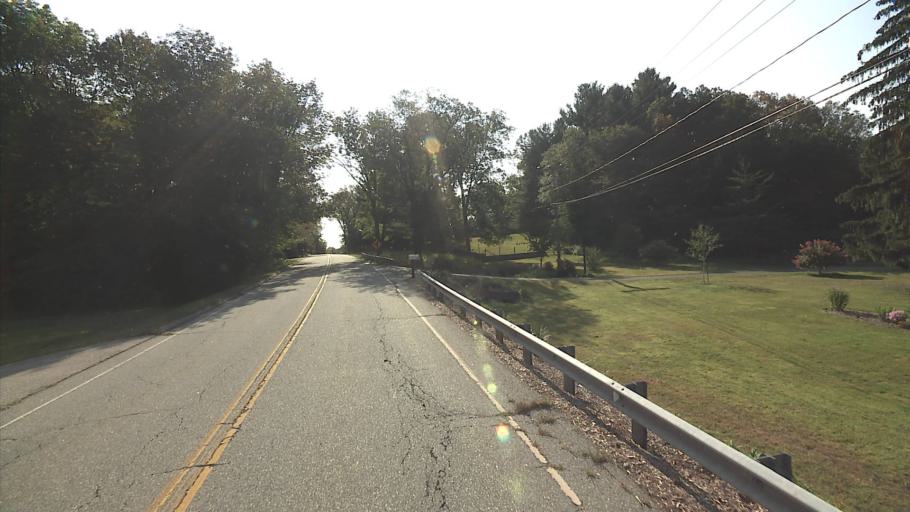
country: US
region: Connecticut
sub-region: Windham County
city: Willimantic
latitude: 41.6701
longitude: -72.2623
